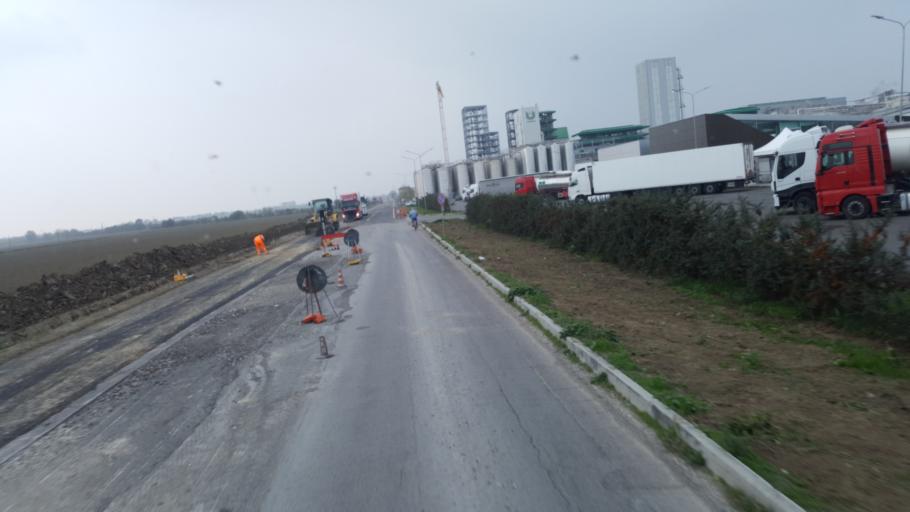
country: IT
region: Emilia-Romagna
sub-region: Provincia di Ravenna
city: Lavezzola
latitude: 44.5330
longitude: 11.8611
